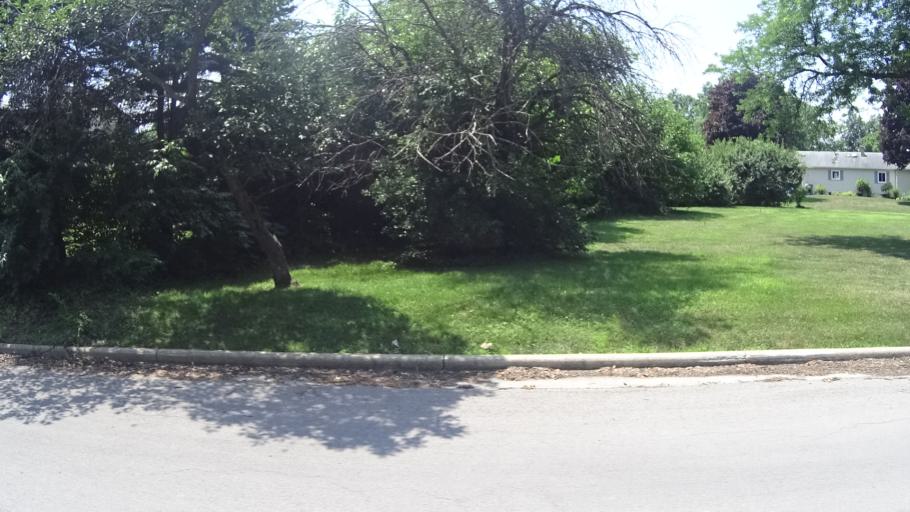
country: US
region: Ohio
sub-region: Erie County
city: Huron
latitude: 41.4086
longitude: -82.6351
